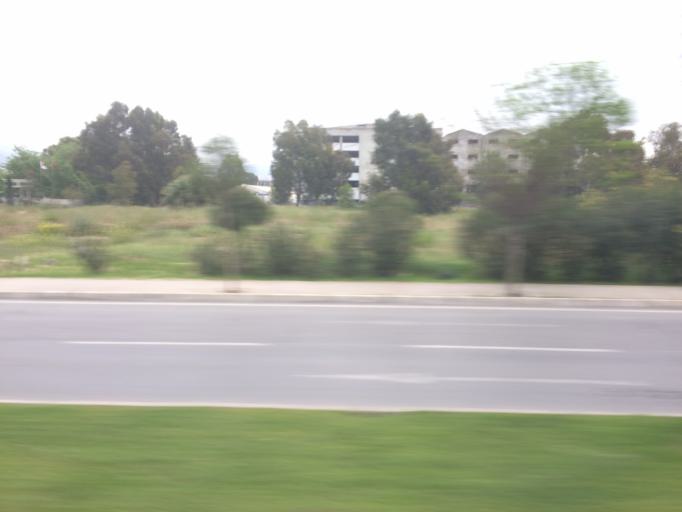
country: TR
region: Izmir
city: Izmir
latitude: 38.4556
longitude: 27.1676
